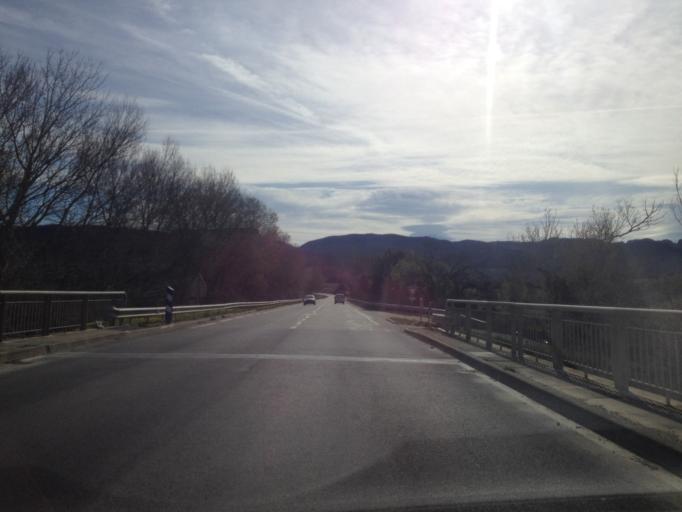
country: FR
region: Provence-Alpes-Cote d'Azur
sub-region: Departement du Vaucluse
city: Sablet
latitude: 44.1943
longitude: 4.9842
